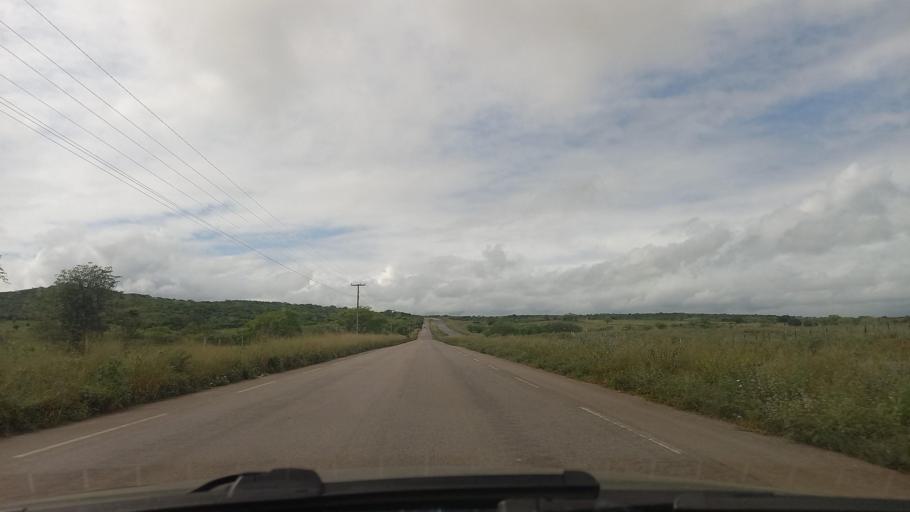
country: BR
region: Alagoas
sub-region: Batalha
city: Batalha
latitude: -9.6563
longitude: -37.1770
